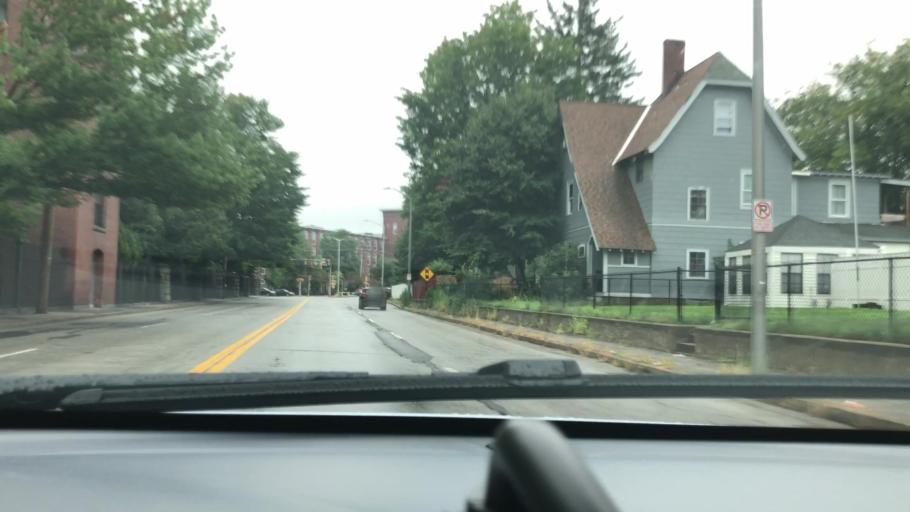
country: US
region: New Hampshire
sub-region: Hillsborough County
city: Manchester
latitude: 42.9951
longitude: -71.4737
